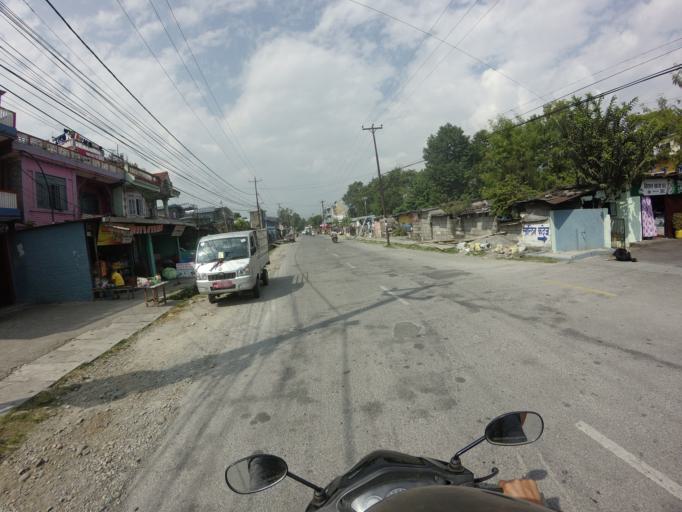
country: NP
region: Western Region
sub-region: Gandaki Zone
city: Pokhara
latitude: 28.2110
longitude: 84.0003
